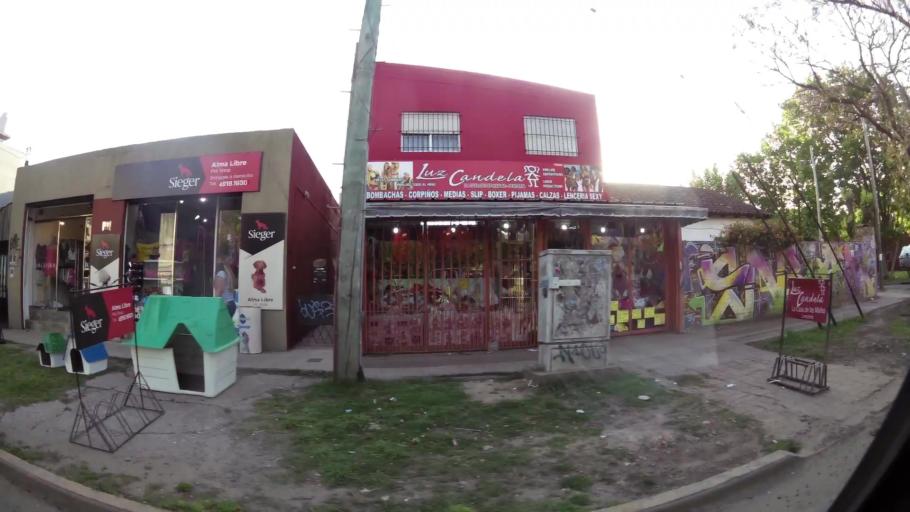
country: AR
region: Buenos Aires
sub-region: Partido de Almirante Brown
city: Adrogue
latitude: -34.7948
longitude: -58.3580
